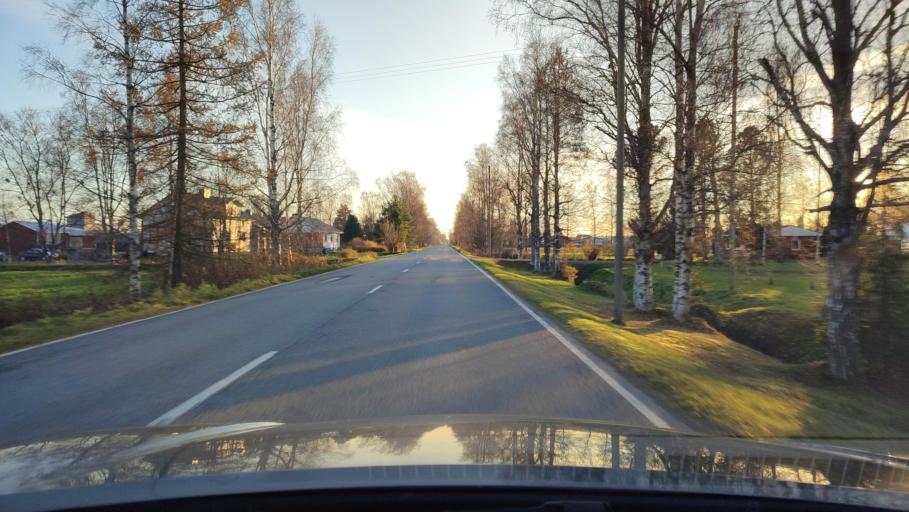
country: FI
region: Ostrobothnia
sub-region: Sydosterbotten
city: Naerpes
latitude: 62.5532
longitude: 21.4051
